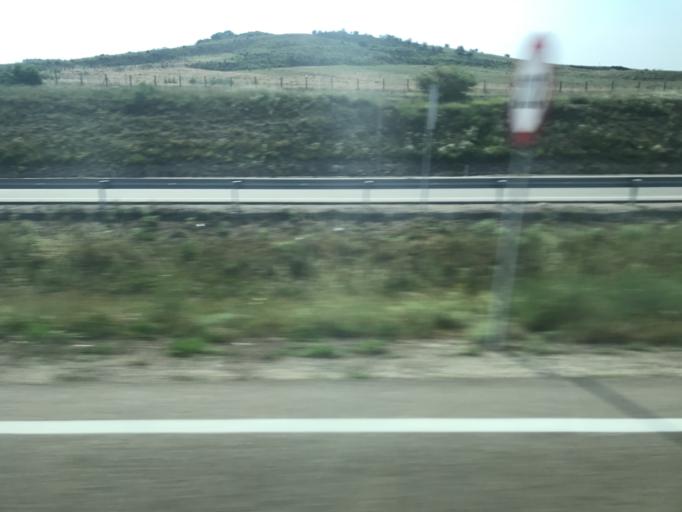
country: ES
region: Castille and Leon
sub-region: Provincia de Burgos
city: Cardenajimeno
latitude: 42.3533
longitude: -3.6027
